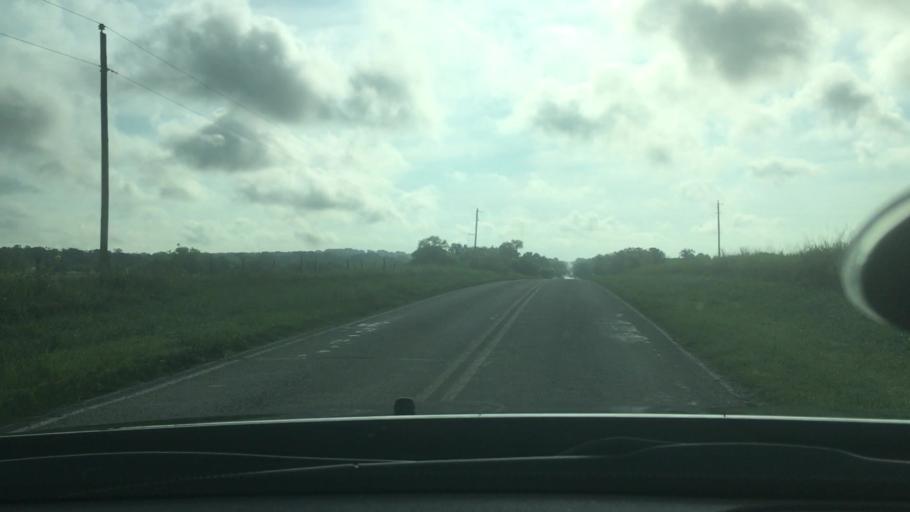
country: US
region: Oklahoma
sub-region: Pontotoc County
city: Ada
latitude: 34.6946
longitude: -96.5357
